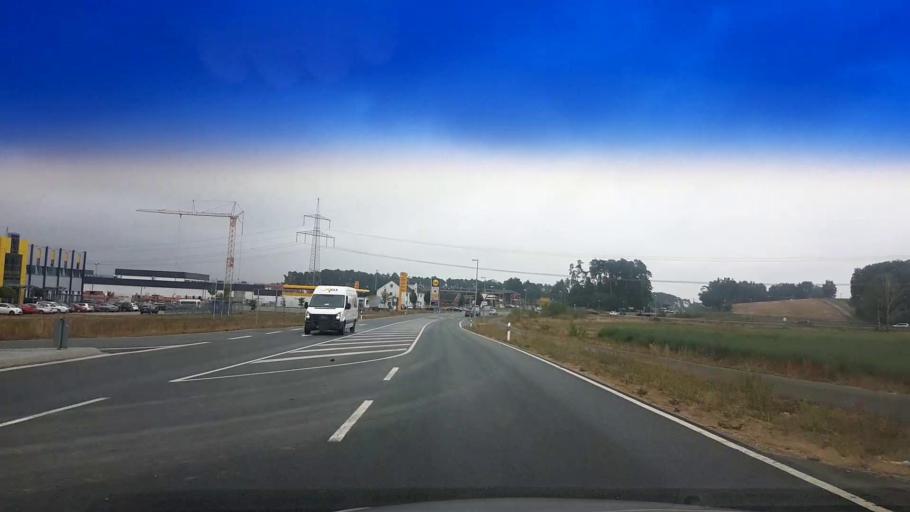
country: DE
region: Bavaria
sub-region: Upper Franconia
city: Hausen
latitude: 49.7040
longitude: 11.0417
